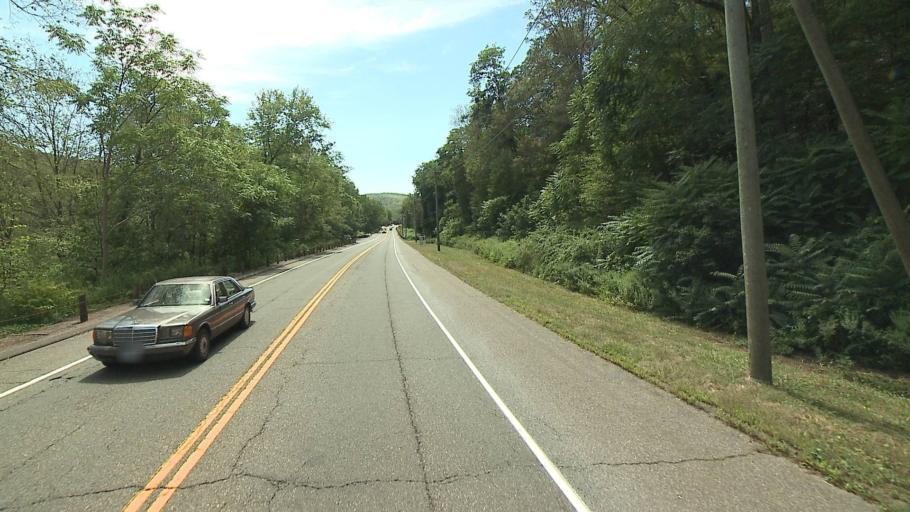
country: US
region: Connecticut
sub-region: Hartford County
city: Collinsville
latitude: 41.7961
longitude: -72.9258
